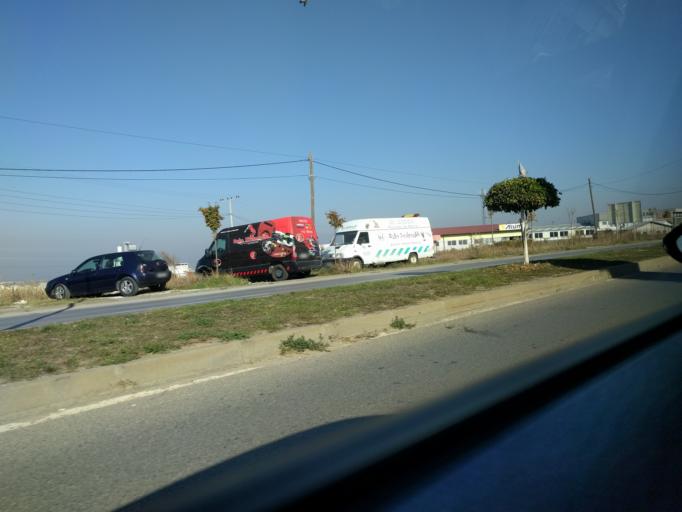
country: XK
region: Prizren
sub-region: Prizren
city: Prizren
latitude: 42.2350
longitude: 20.7593
